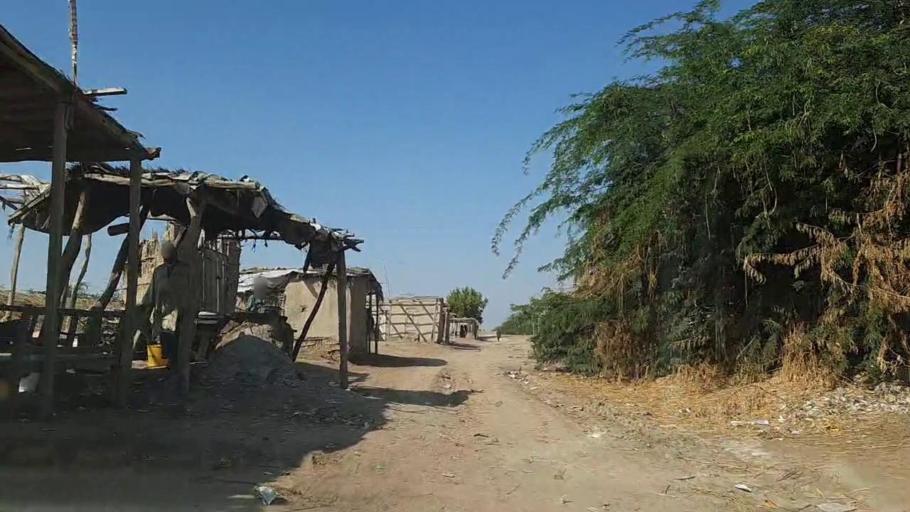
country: PK
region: Sindh
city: Chuhar Jamali
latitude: 24.5475
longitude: 68.0156
